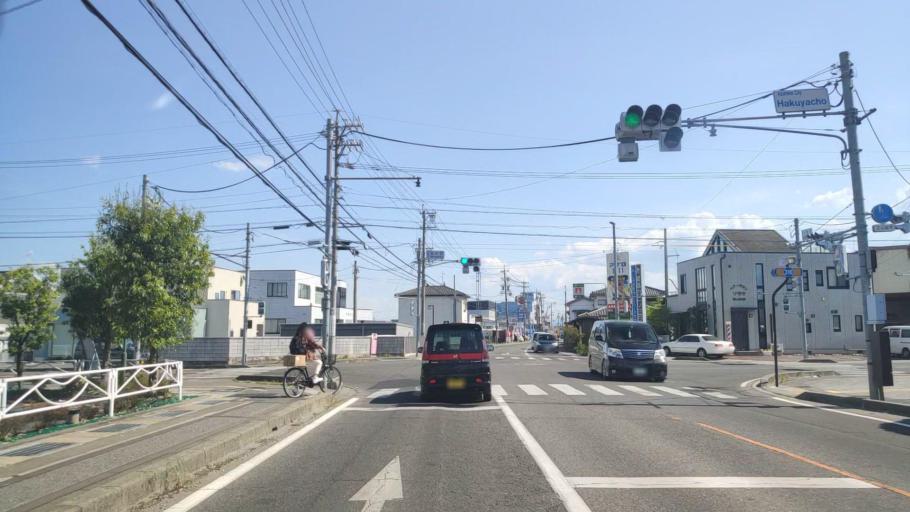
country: JP
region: Nagano
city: Hotaka
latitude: 36.3243
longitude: 137.8934
